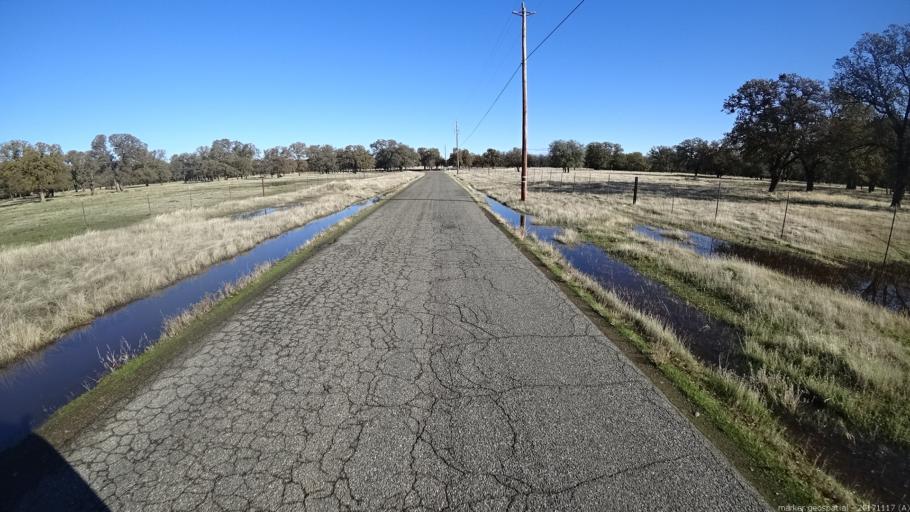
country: US
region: California
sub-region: Shasta County
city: Anderson
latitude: 40.4621
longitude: -122.1920
